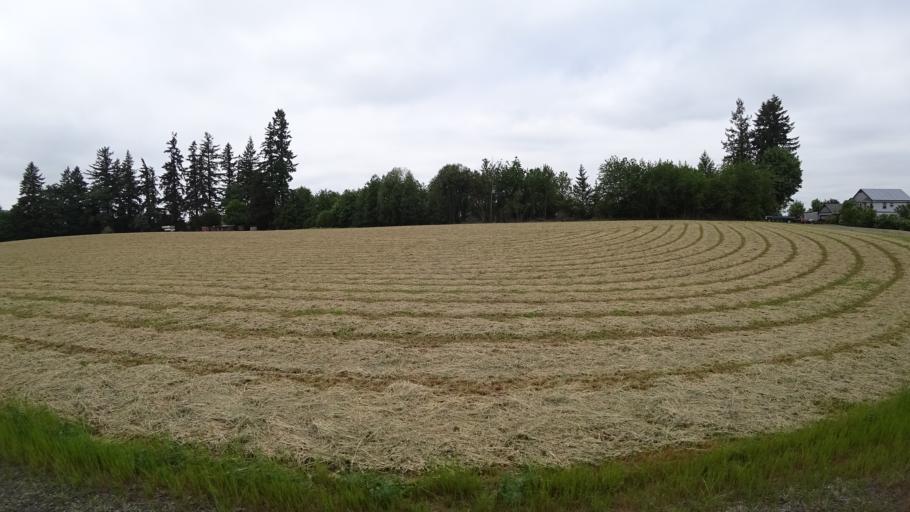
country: US
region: Oregon
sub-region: Washington County
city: Hillsboro
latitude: 45.4946
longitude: -122.9872
